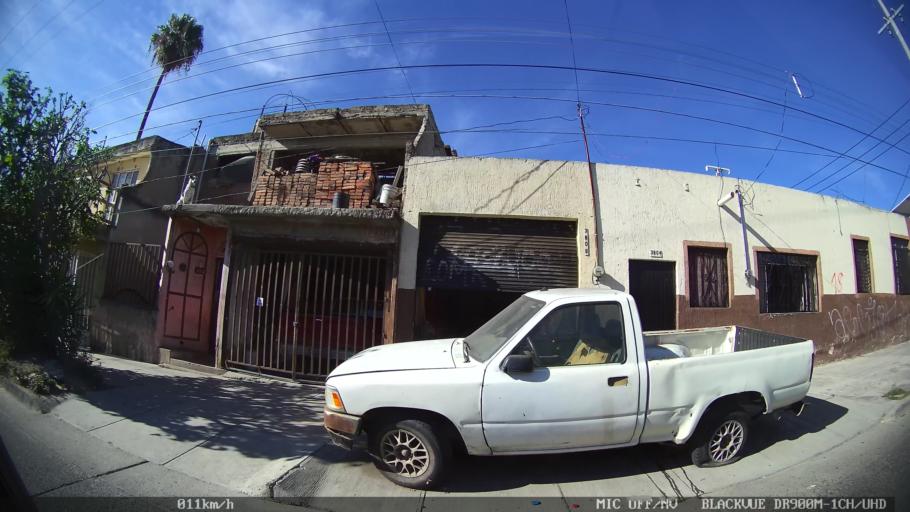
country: MX
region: Jalisco
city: Tlaquepaque
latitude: 20.6965
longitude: -103.2776
